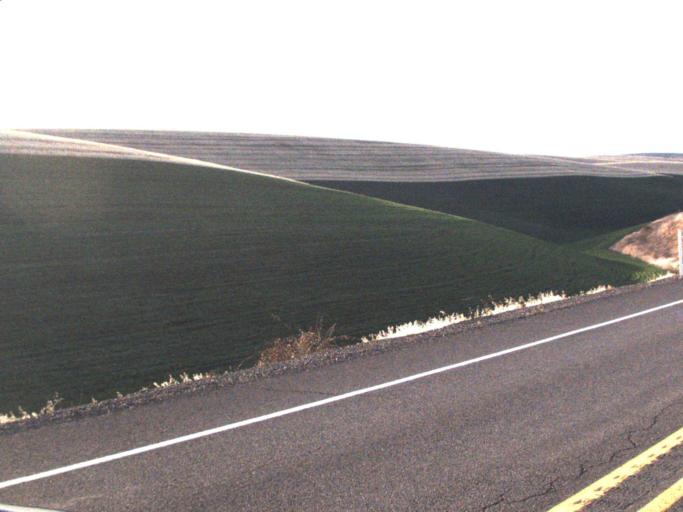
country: US
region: Washington
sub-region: Garfield County
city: Pomeroy
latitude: 46.7088
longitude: -117.7842
